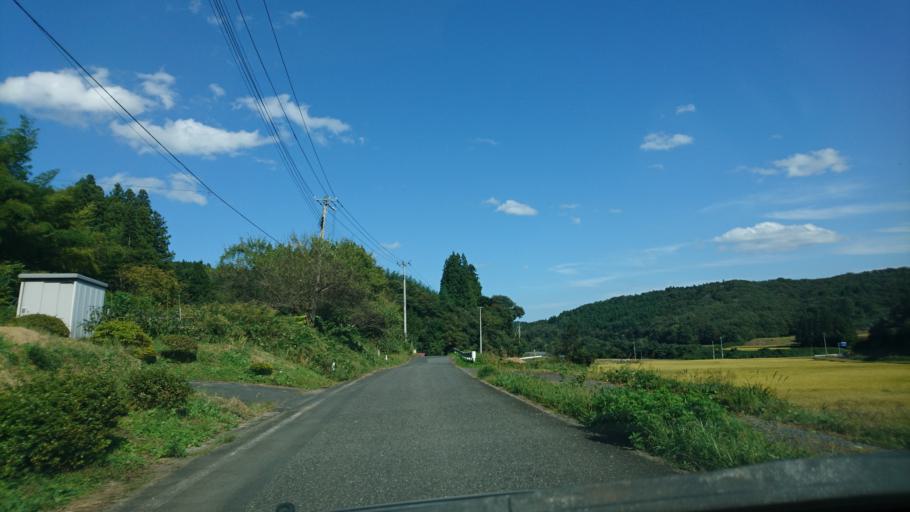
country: JP
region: Iwate
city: Ichinoseki
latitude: 38.8941
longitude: 141.0298
